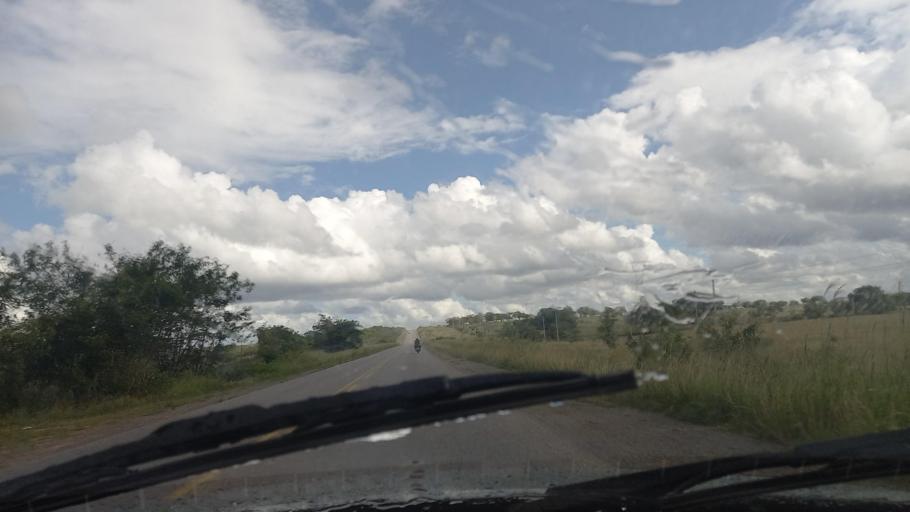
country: BR
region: Pernambuco
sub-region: Lajedo
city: Lajedo
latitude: -8.5823
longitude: -36.2881
